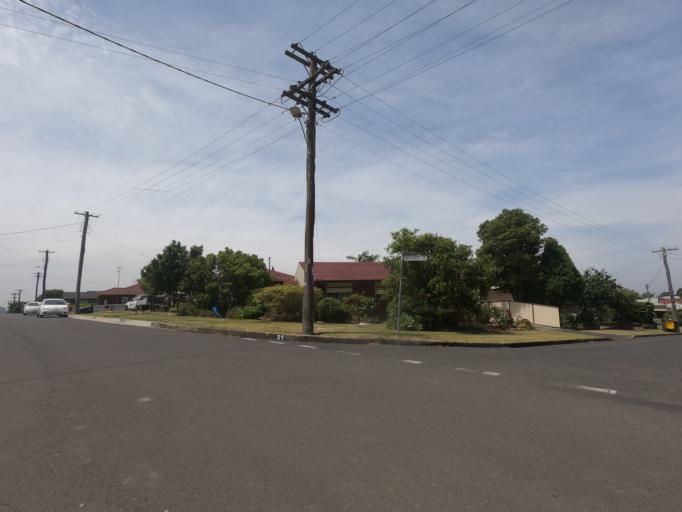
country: AU
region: New South Wales
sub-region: Wollongong
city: Mount Ousley
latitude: -34.3926
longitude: 150.8828
